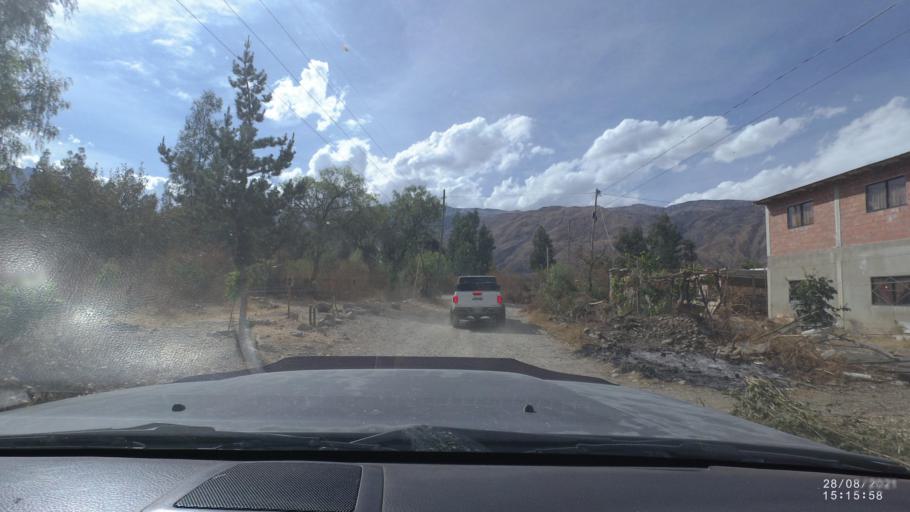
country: BO
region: Cochabamba
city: Cochabamba
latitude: -17.3325
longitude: -66.2544
